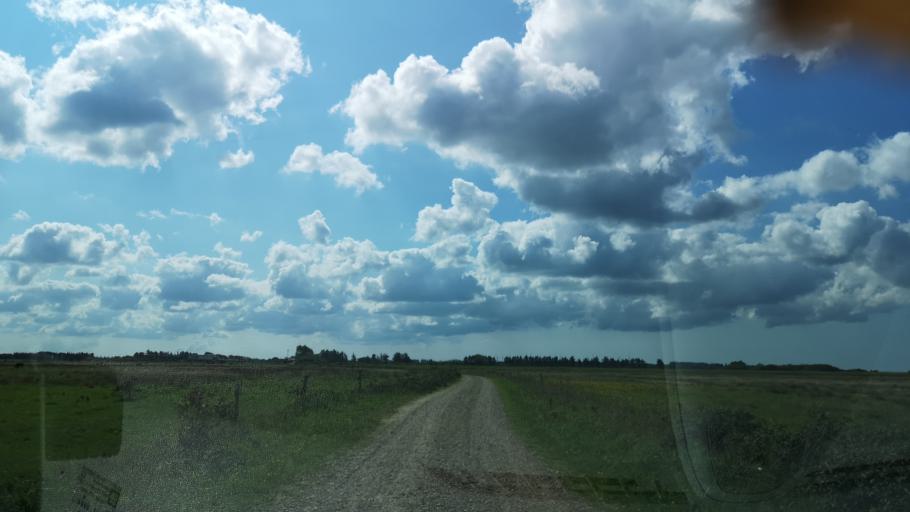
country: DK
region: Central Jutland
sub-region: Ringkobing-Skjern Kommune
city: Skjern
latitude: 55.9099
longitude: 8.4012
